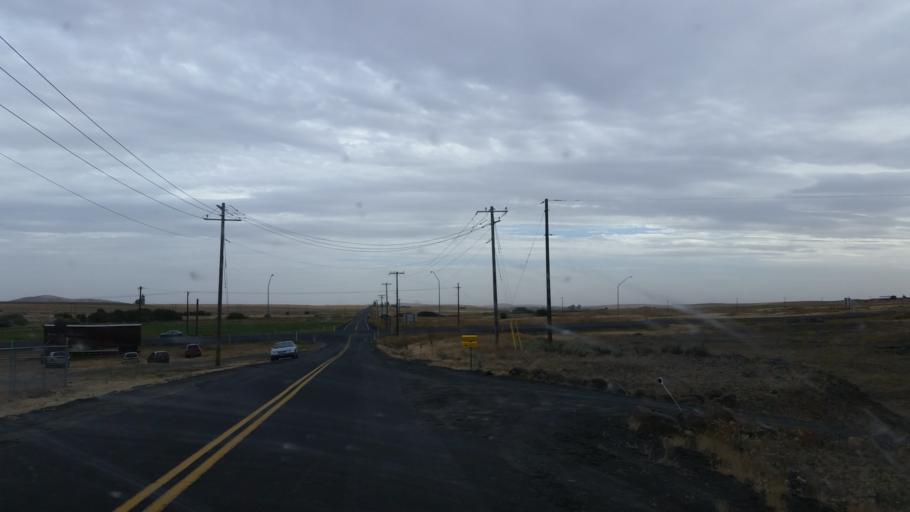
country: US
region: Washington
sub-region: Lincoln County
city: Davenport
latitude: 47.6621
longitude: -117.9380
